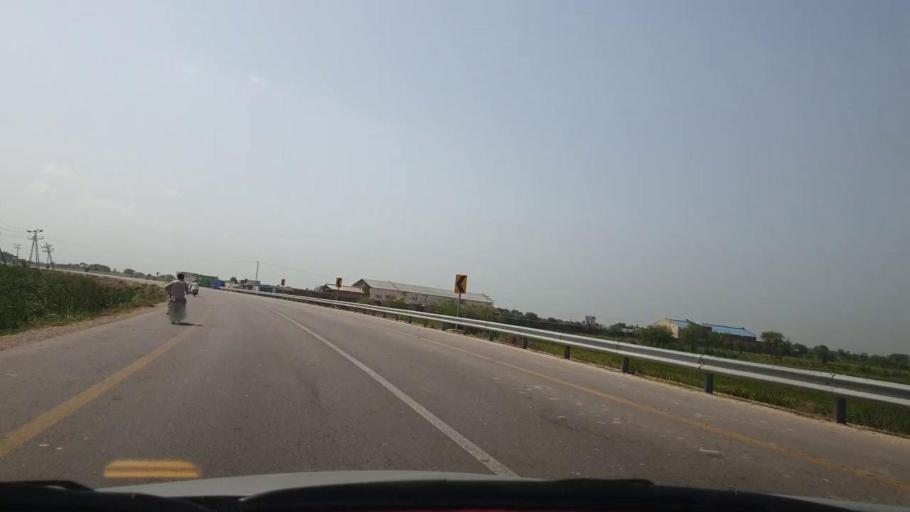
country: PK
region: Sindh
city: Matli
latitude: 25.0047
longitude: 68.6501
